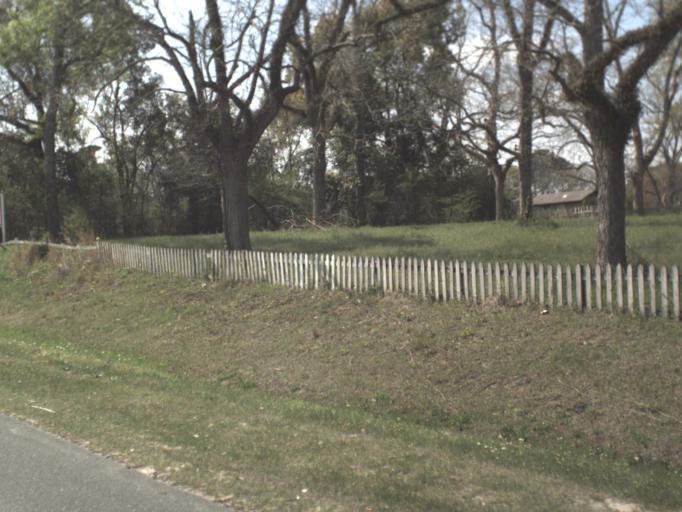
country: US
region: Florida
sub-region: Gadsden County
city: Havana
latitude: 30.6427
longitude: -84.4170
